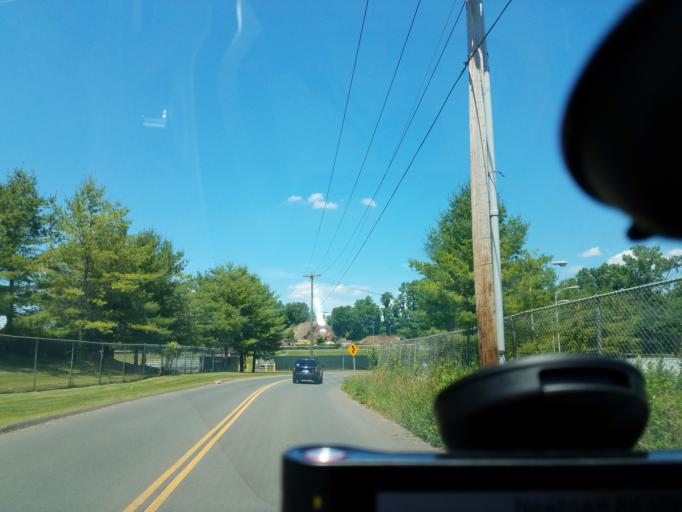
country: US
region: Connecticut
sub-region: Fairfield County
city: Bethel
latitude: 41.4014
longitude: -73.4154
